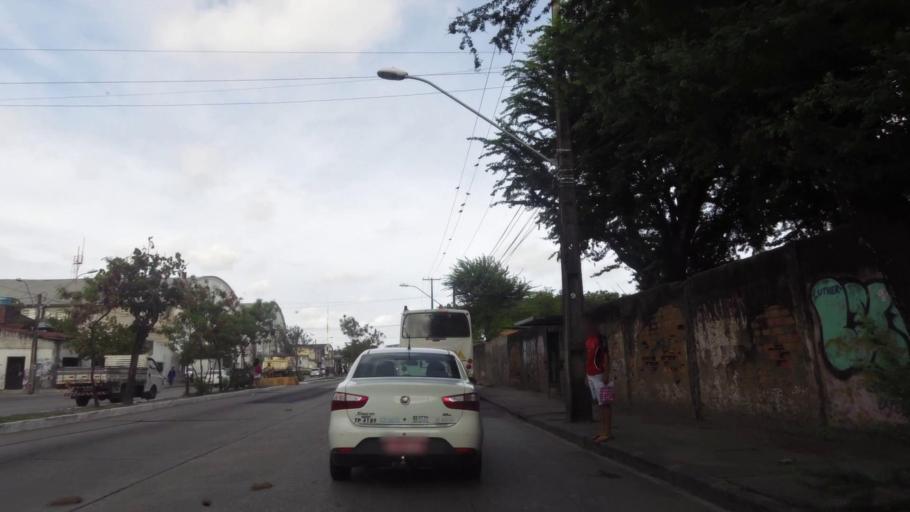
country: BR
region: Pernambuco
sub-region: Recife
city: Recife
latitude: -8.0782
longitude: -34.8985
